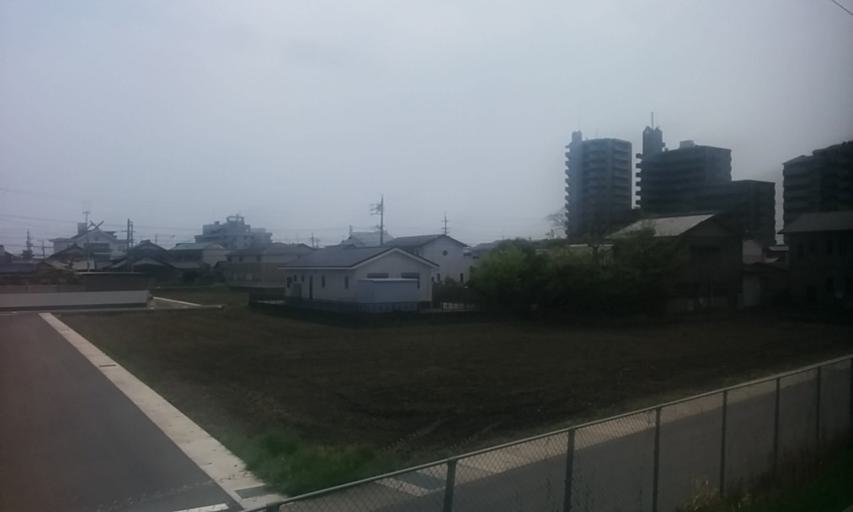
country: JP
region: Aichi
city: Kuroda
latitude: 35.3529
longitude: 136.7799
